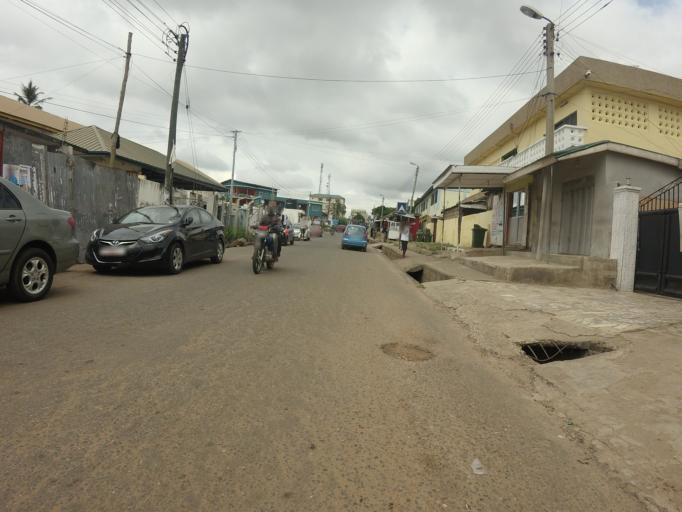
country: GH
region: Greater Accra
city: Accra
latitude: 5.5895
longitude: -0.2019
